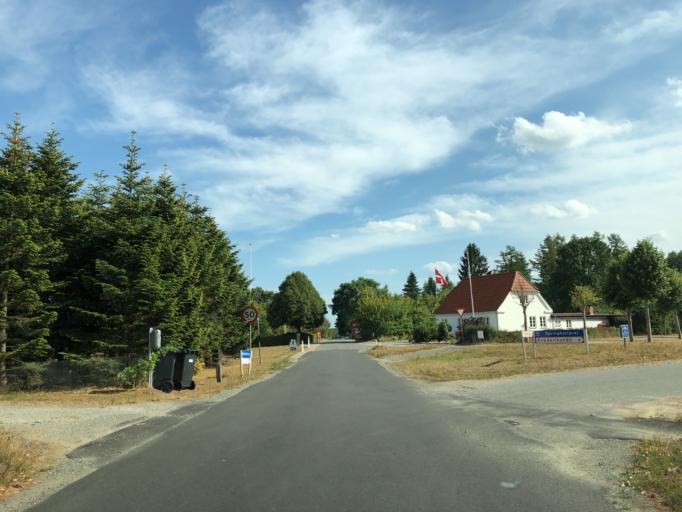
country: DK
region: South Denmark
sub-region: Vejle Kommune
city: Egtved
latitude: 55.6581
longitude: 9.2593
